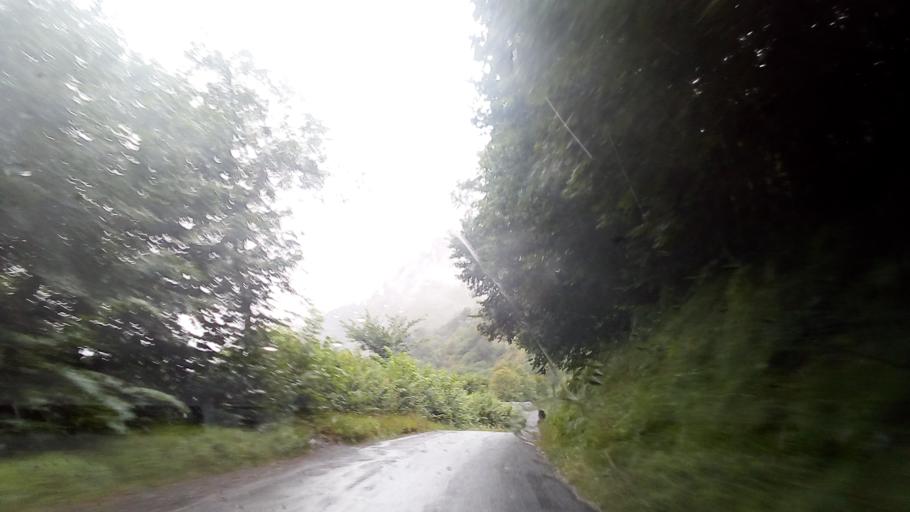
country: FR
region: Midi-Pyrenees
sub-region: Departement des Hautes-Pyrenees
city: Cauterets
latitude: 42.9464
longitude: -0.2235
